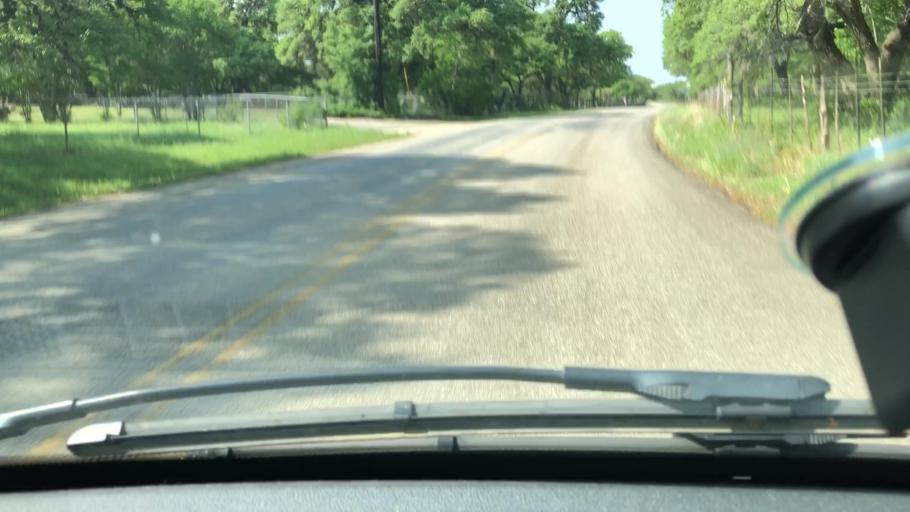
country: US
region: Texas
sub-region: Comal County
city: Bulverde
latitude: 29.7610
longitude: -98.4587
